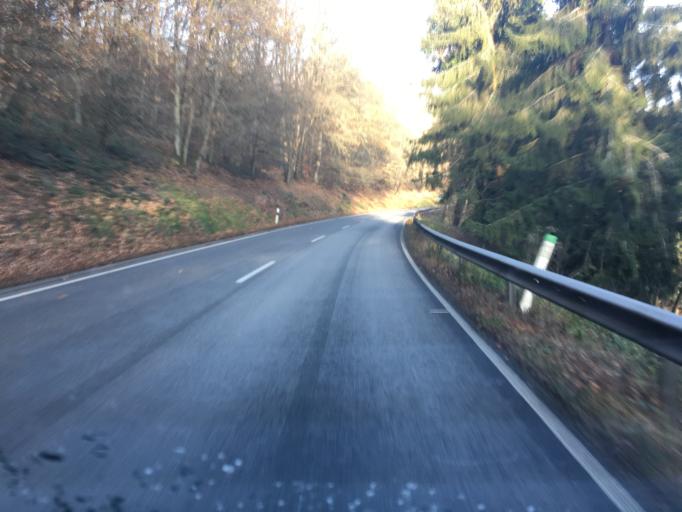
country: DE
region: North Rhine-Westphalia
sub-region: Regierungsbezirk Koln
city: Schleiden
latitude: 50.5694
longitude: 6.4867
